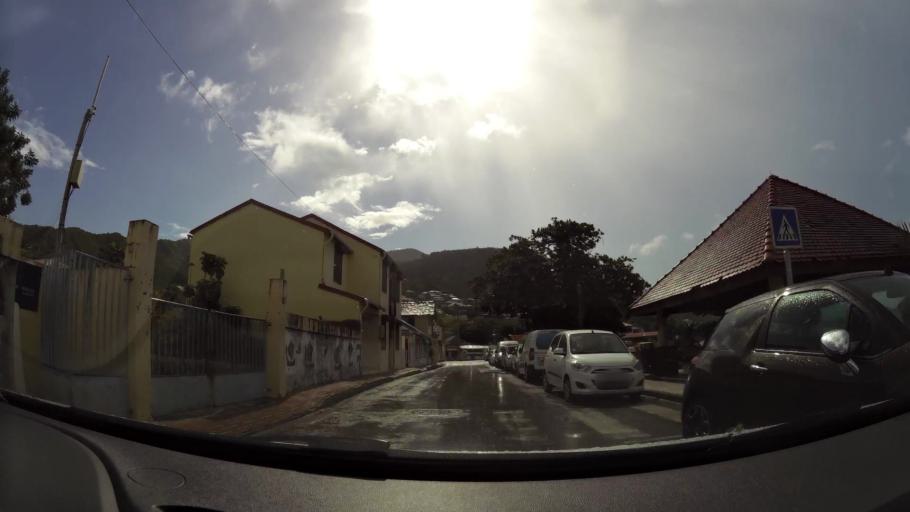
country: MQ
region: Martinique
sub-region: Martinique
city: Les Trois-Ilets
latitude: 14.4901
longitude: -61.0799
